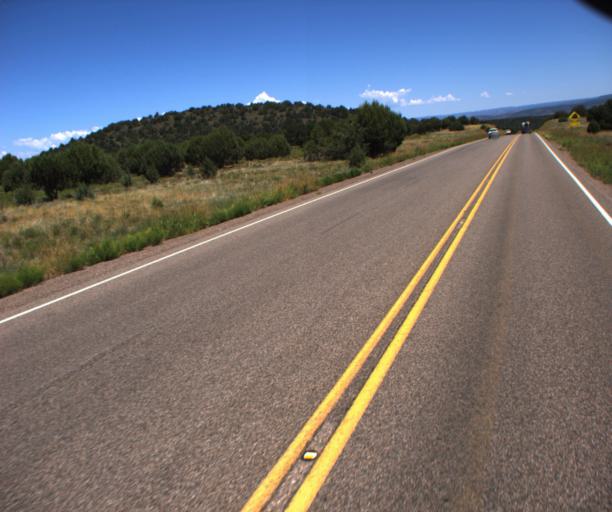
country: US
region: Arizona
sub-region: Navajo County
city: Cibecue
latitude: 33.7184
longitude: -110.5330
